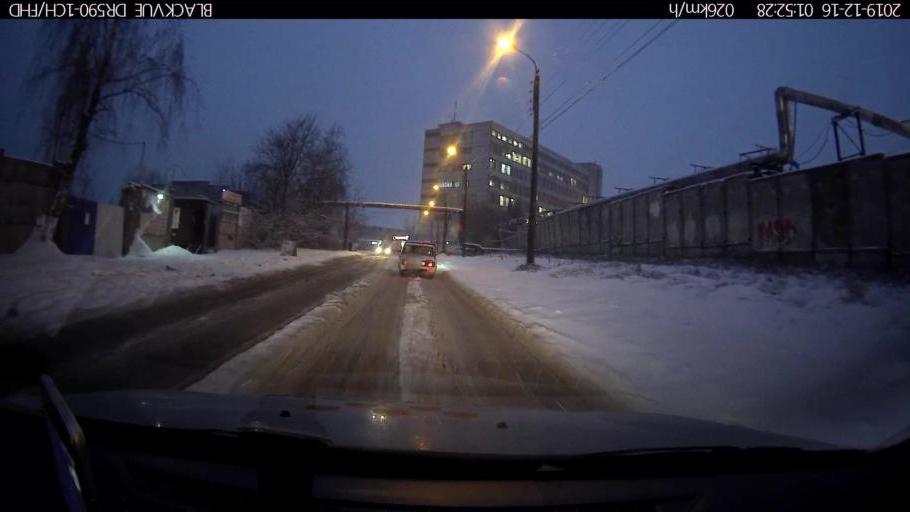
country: RU
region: Nizjnij Novgorod
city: Nizhniy Novgorod
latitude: 56.2887
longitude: 44.0012
